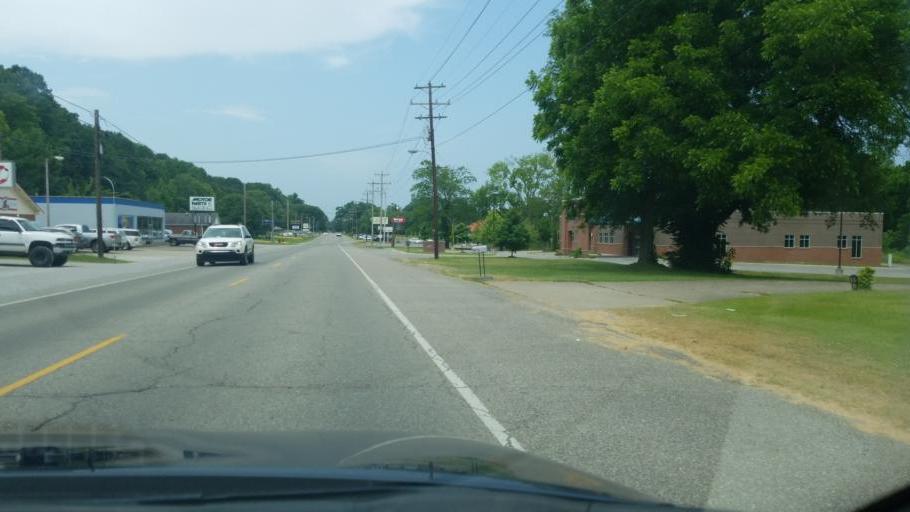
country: US
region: Tennessee
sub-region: Humphreys County
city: Waverly
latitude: 36.0836
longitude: -87.8074
